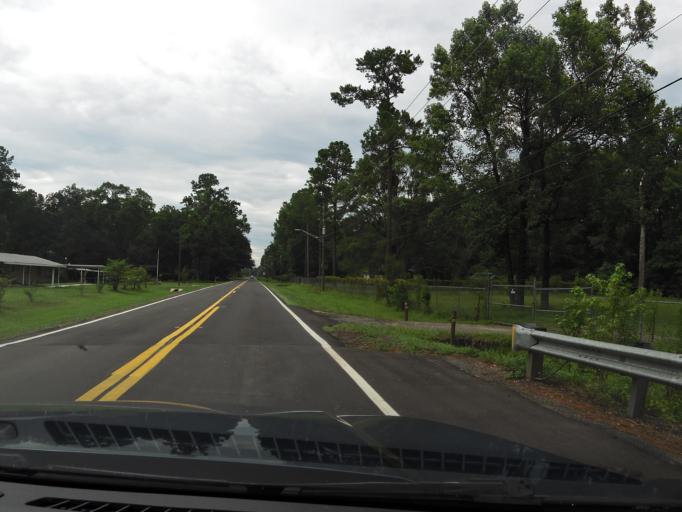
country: US
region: Florida
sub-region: Nassau County
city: Nassau Village-Ratliff
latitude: 30.4411
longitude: -81.7725
